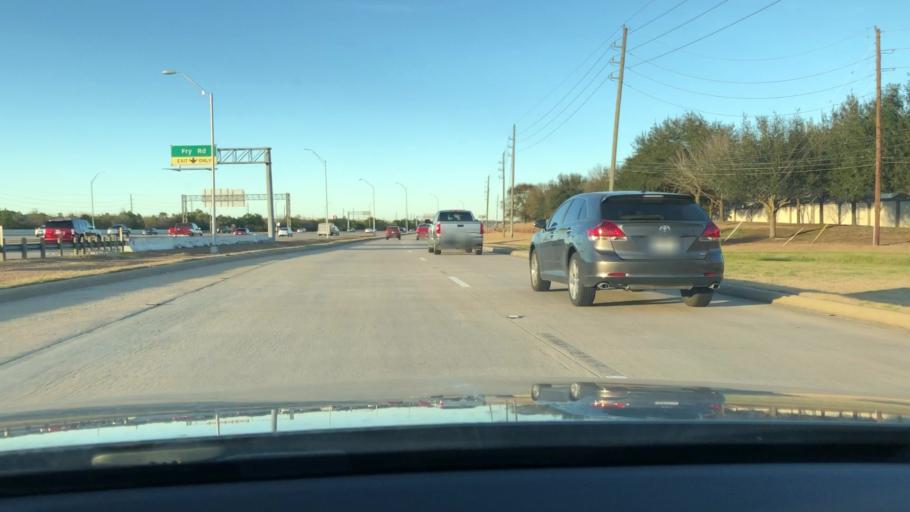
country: US
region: Texas
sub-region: Fort Bend County
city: Cinco Ranch
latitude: 29.7060
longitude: -95.7758
